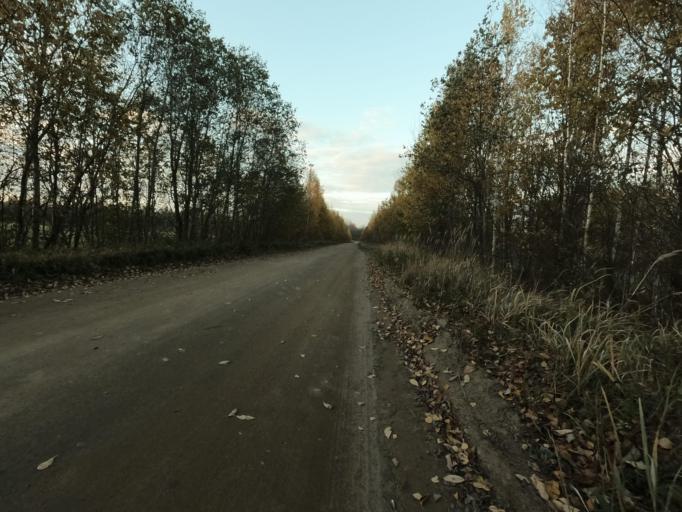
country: RU
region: Leningrad
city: Mga
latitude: 59.8037
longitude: 31.2007
